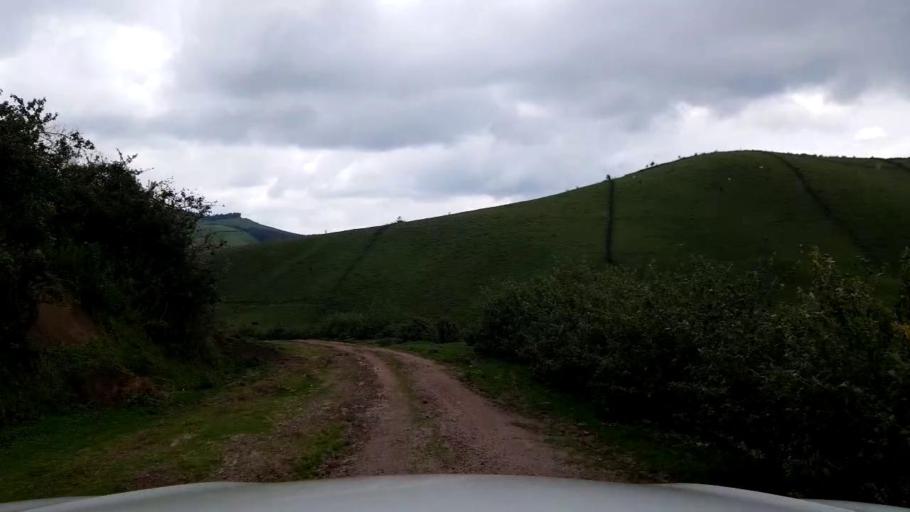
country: RW
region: Western Province
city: Gisenyi
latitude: -1.6806
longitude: 29.4177
